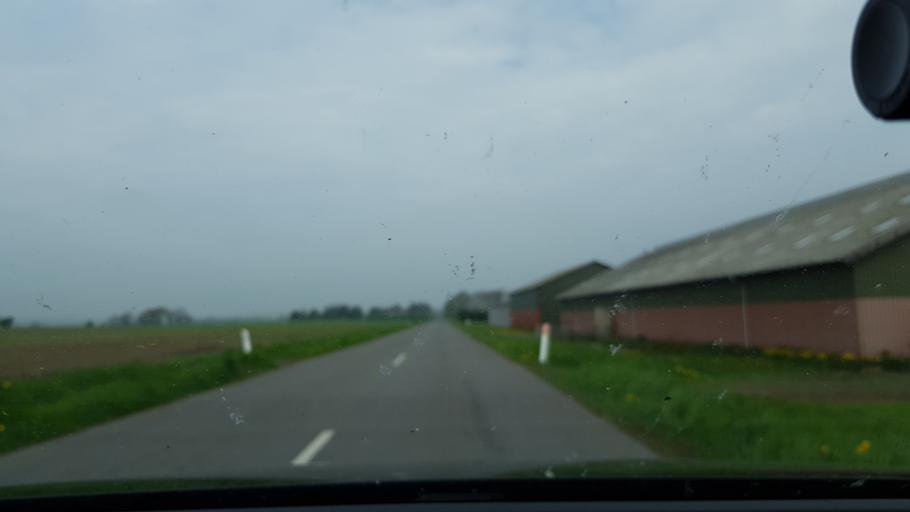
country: DK
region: Capital Region
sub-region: Bornholm Kommune
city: Nexo
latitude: 55.0144
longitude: 15.0961
